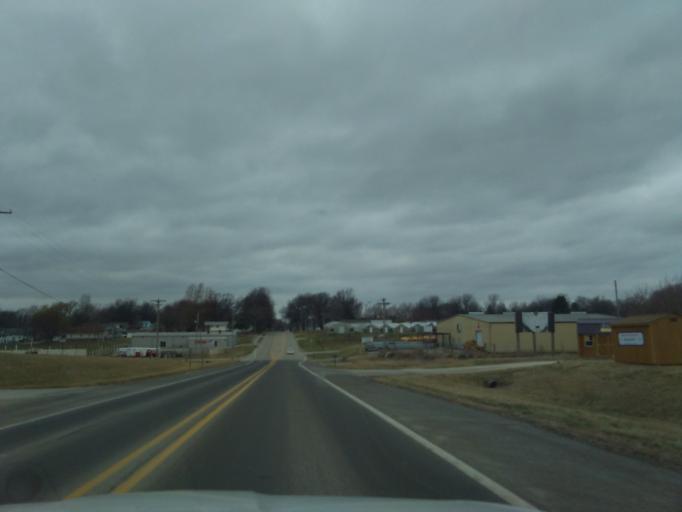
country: US
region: Nebraska
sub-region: Richardson County
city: Falls City
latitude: 40.0584
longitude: -95.5869
